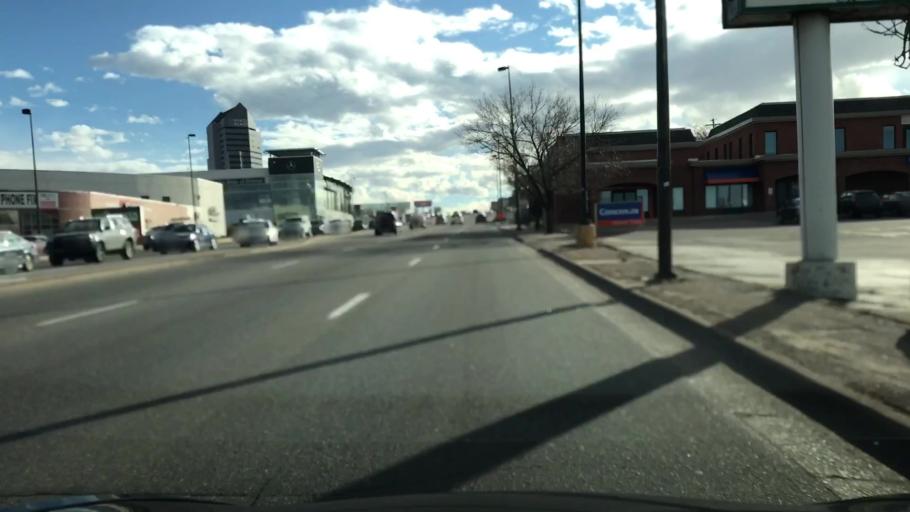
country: US
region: Colorado
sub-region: Arapahoe County
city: Glendale
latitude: 39.7015
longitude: -104.9408
